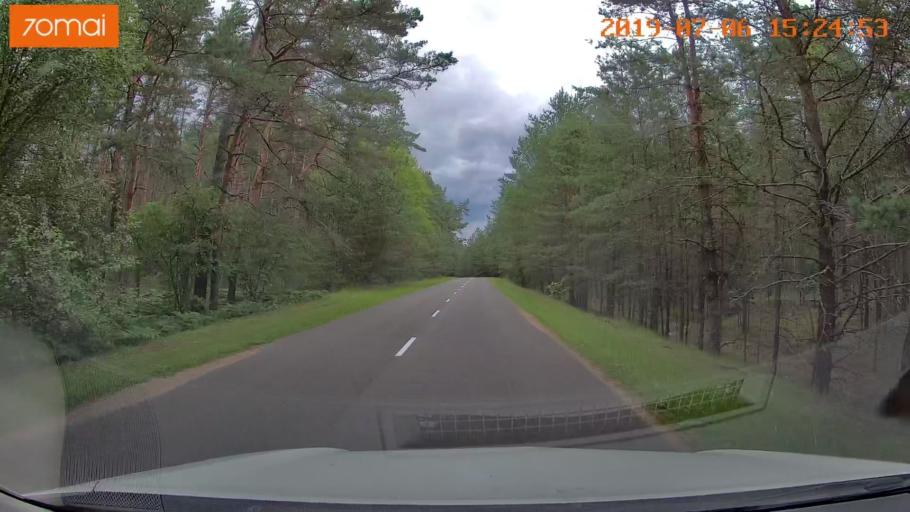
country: BY
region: Minsk
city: Valozhyn
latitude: 54.0250
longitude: 26.6038
